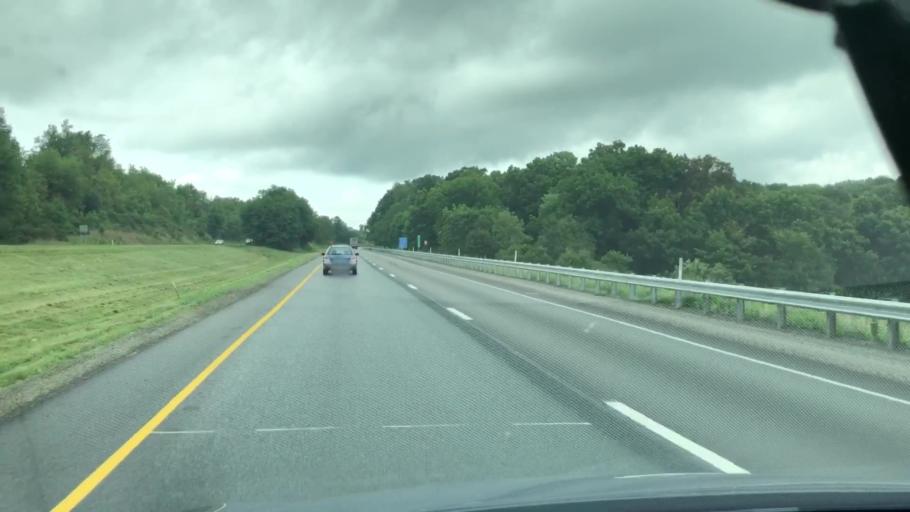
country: US
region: Pennsylvania
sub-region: Butler County
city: Slippery Rock
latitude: 40.9813
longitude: -80.1329
